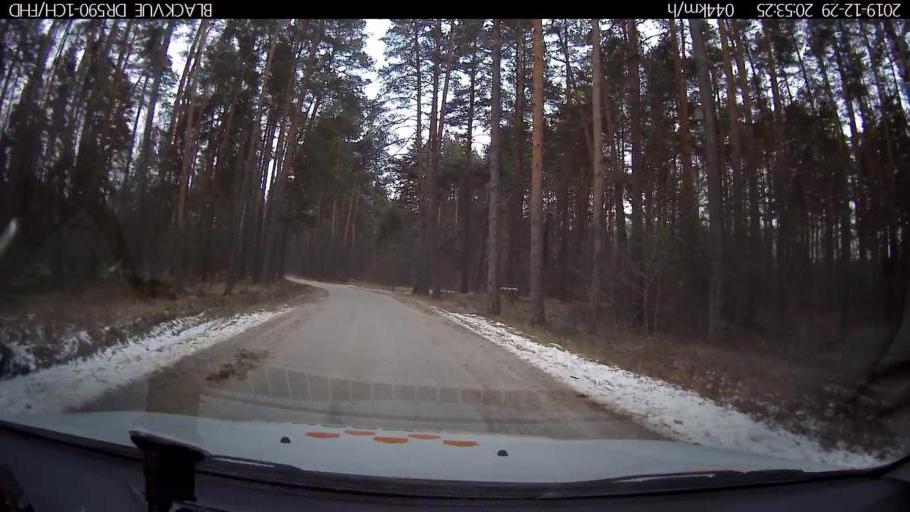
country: RU
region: Nizjnij Novgorod
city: Afonino
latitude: 56.1712
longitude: 43.9867
